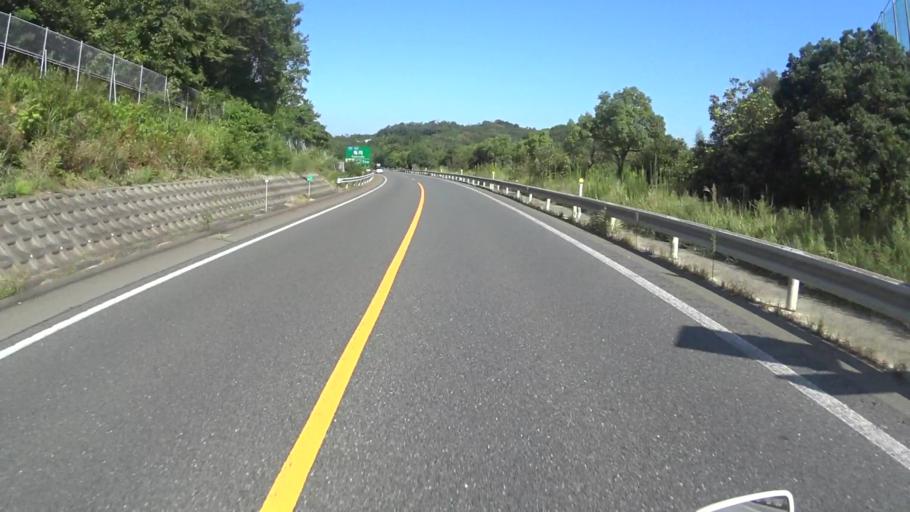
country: JP
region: Kyoto
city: Kameoka
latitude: 34.9986
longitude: 135.5727
